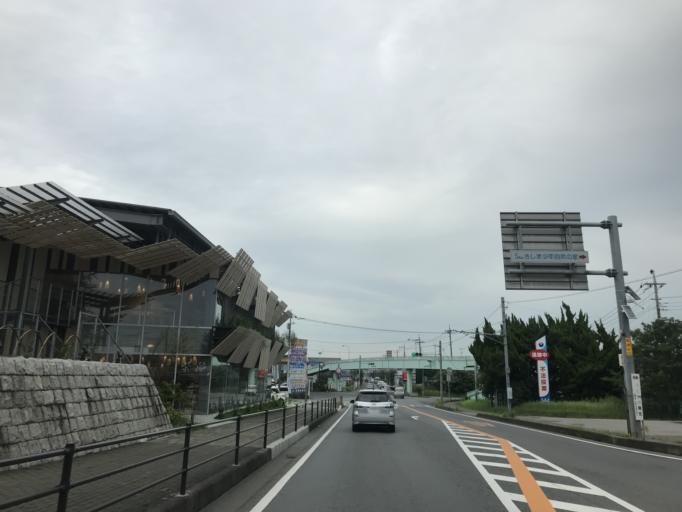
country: JP
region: Ibaraki
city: Sakai
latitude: 36.1029
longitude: 139.7958
